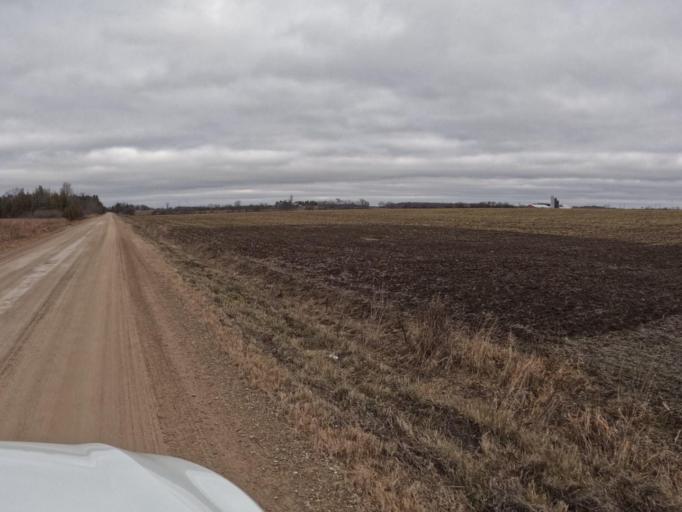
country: CA
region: Ontario
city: Shelburne
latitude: 43.9488
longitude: -80.3963
